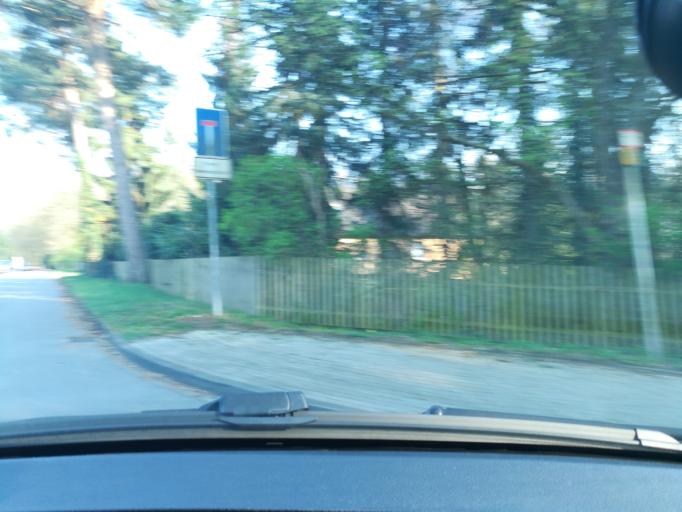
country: DE
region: North Rhine-Westphalia
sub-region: Regierungsbezirk Detmold
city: Bielefeld
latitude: 52.0041
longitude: 8.4757
